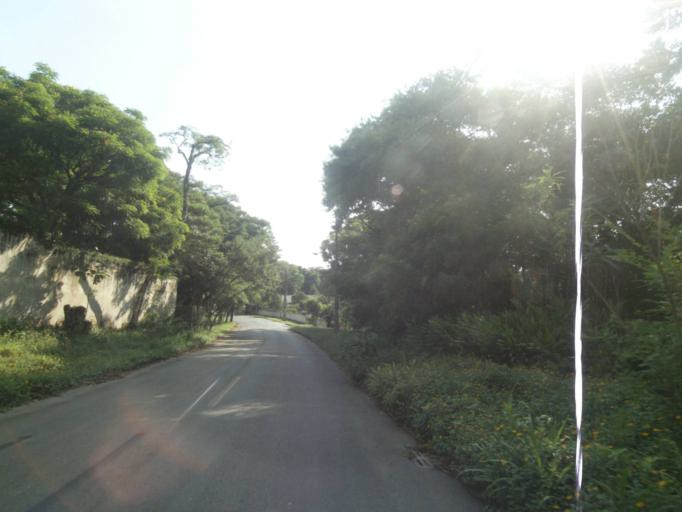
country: BR
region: Parana
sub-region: Curitiba
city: Curitiba
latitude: -25.4097
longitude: -49.3171
